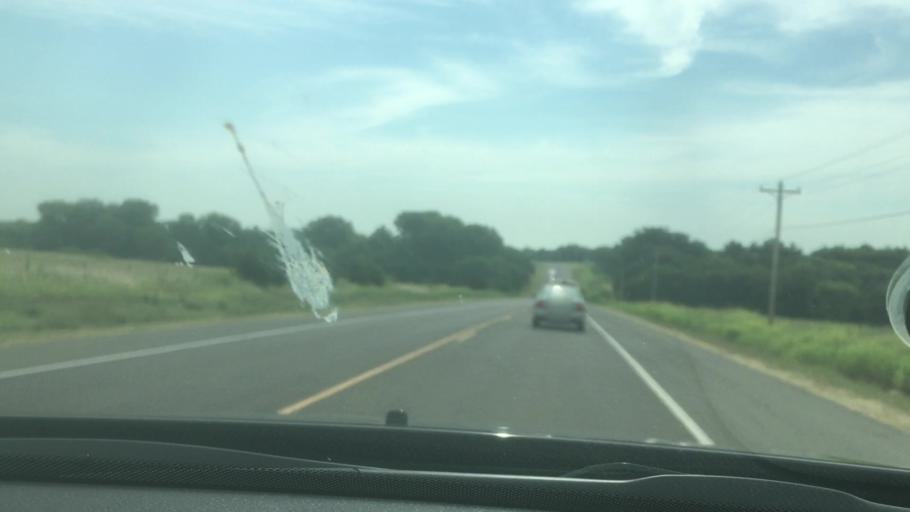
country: US
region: Oklahoma
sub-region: Garvin County
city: Maysville
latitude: 34.8183
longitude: -97.4344
